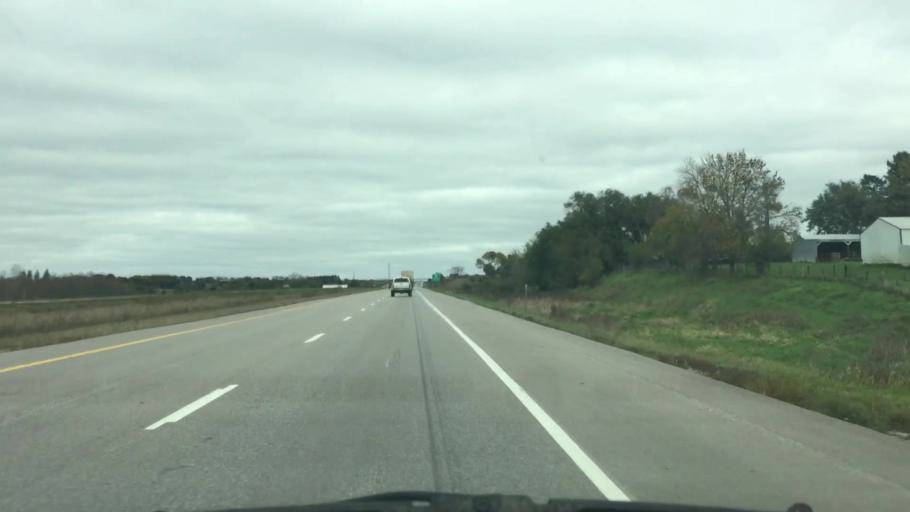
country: US
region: Iowa
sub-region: Warren County
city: Norwalk
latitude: 41.4577
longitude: -93.7797
